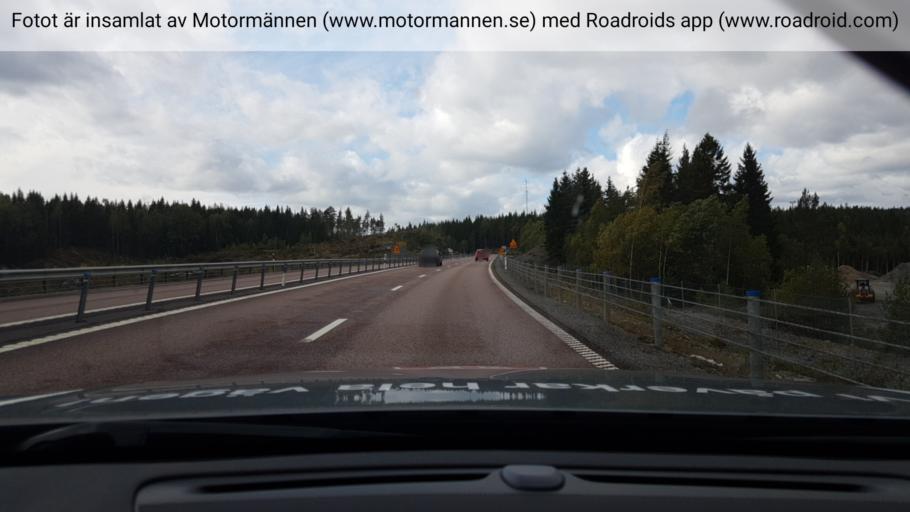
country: SE
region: Vaermland
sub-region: Arjangs Kommun
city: Toecksfors
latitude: 59.4889
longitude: 11.7620
